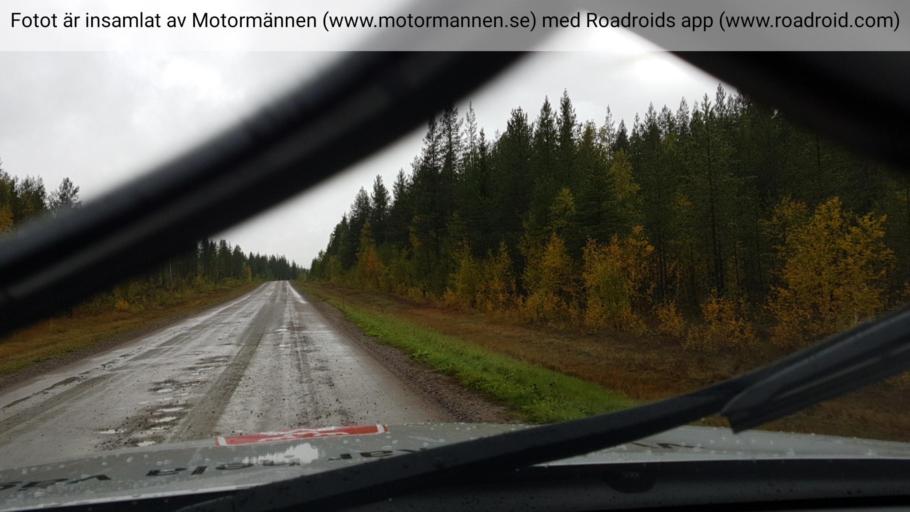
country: SE
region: Norrbotten
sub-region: Alvsbyns Kommun
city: AElvsbyn
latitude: 66.2651
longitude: 21.0503
